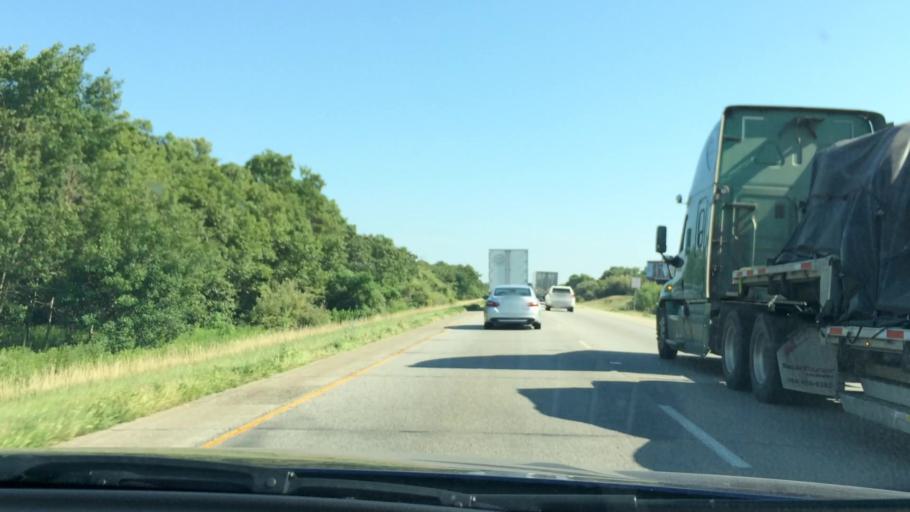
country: US
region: Indiana
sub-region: Newton County
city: Roselawn
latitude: 41.0276
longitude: -87.2702
